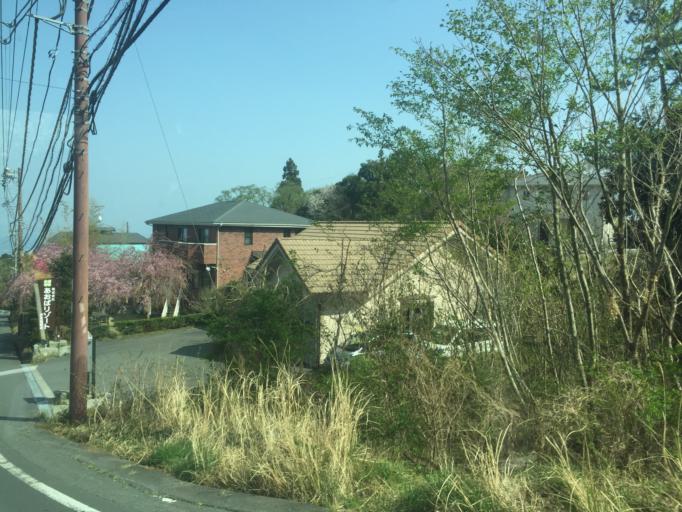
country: JP
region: Shizuoka
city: Ito
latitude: 34.9052
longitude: 139.1045
